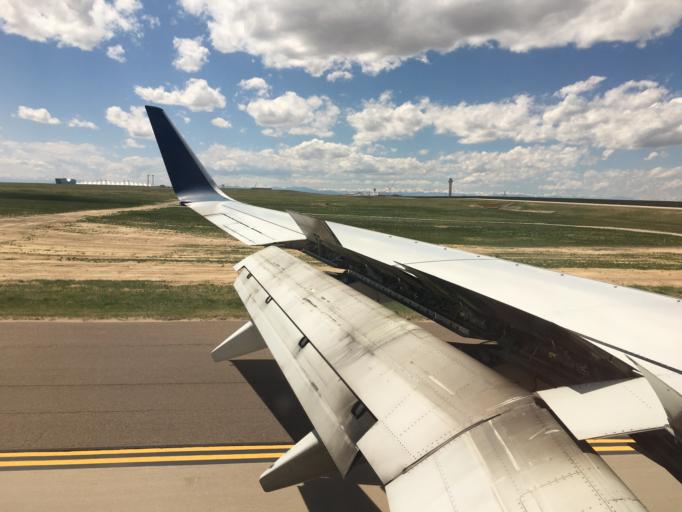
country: US
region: Colorado
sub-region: Weld County
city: Lochbuie
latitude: 39.8551
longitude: -104.6439
